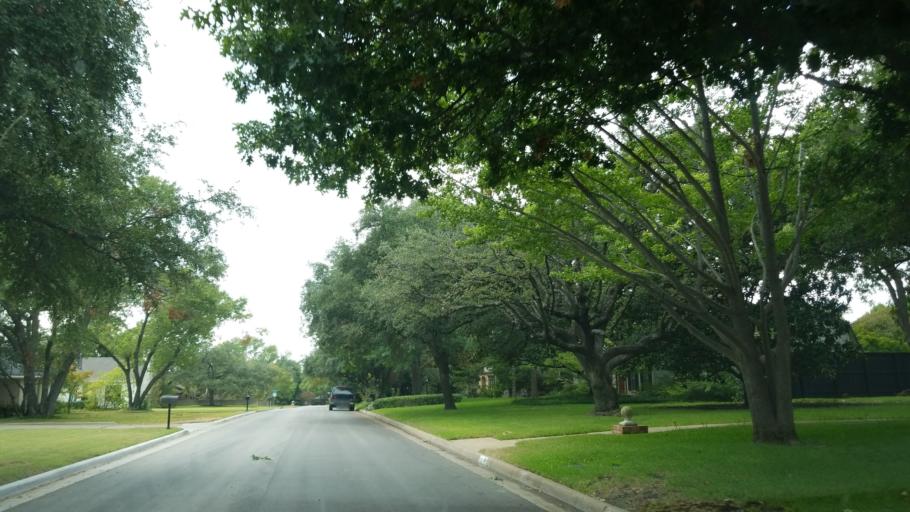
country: US
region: Texas
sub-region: Dallas County
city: Addison
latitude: 32.9457
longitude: -96.7844
